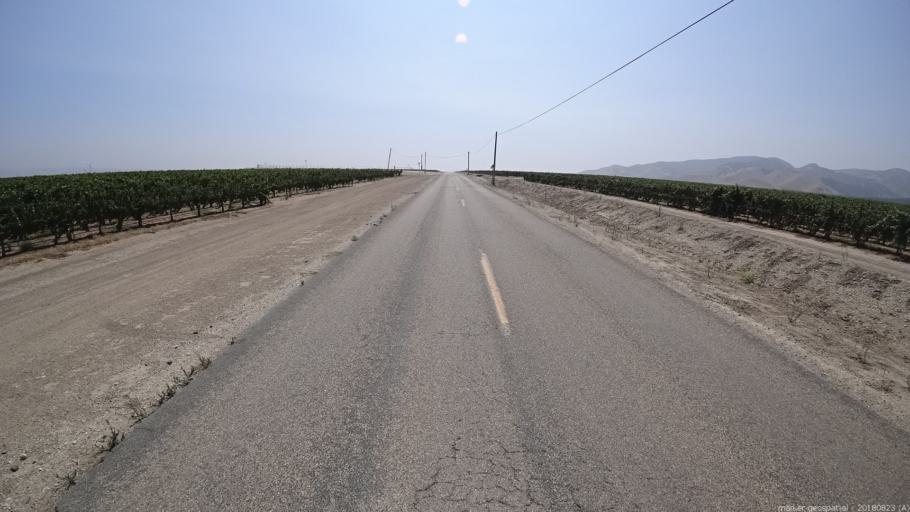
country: US
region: California
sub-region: Monterey County
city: Greenfield
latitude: 36.2736
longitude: -121.2228
